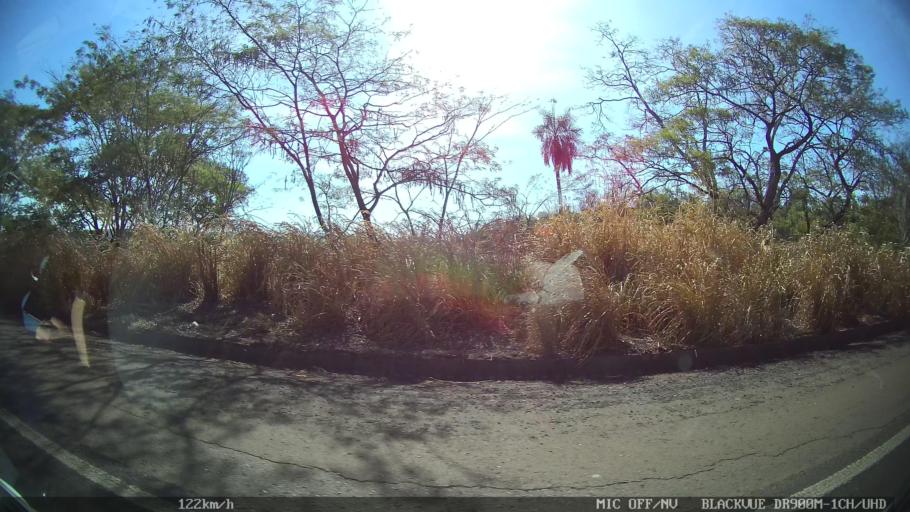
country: BR
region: Sao Paulo
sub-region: Barretos
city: Barretos
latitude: -20.6005
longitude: -48.7265
